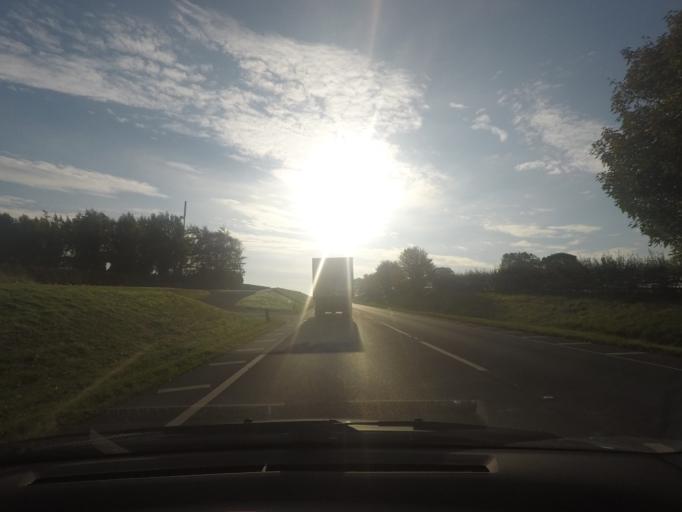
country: GB
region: England
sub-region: East Riding of Yorkshire
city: Hayton
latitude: 53.8850
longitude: -0.7247
